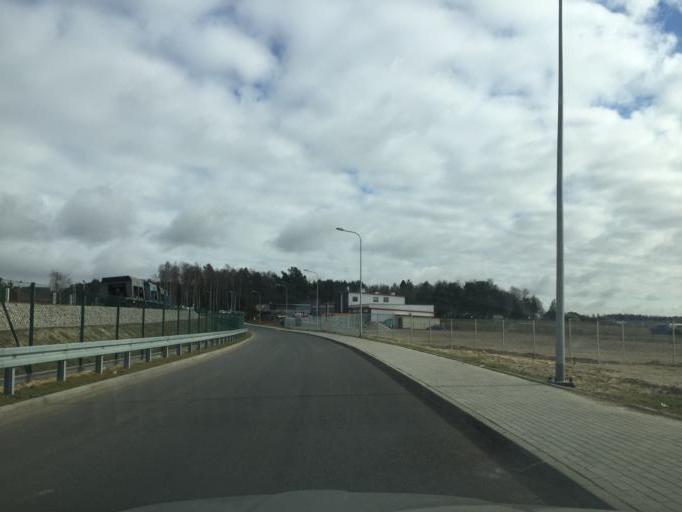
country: PL
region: Pomeranian Voivodeship
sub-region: Powiat kartuski
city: Banino
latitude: 54.3791
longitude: 18.4825
